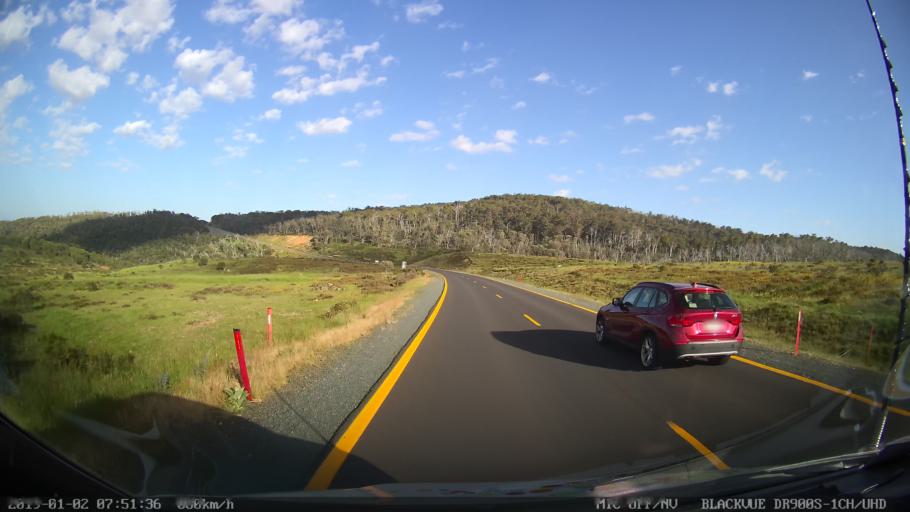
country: AU
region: New South Wales
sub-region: Tumut Shire
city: Tumut
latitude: -35.7167
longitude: 148.5298
